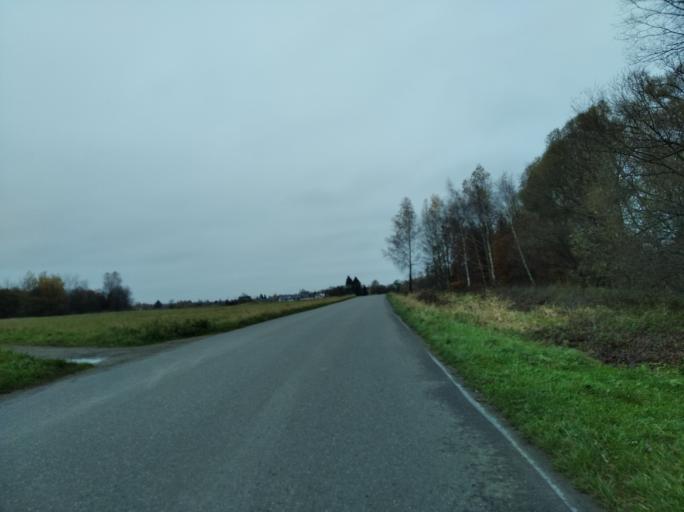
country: PL
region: Subcarpathian Voivodeship
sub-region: Powiat krosnienski
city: Chorkowka
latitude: 49.6771
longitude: 21.6799
